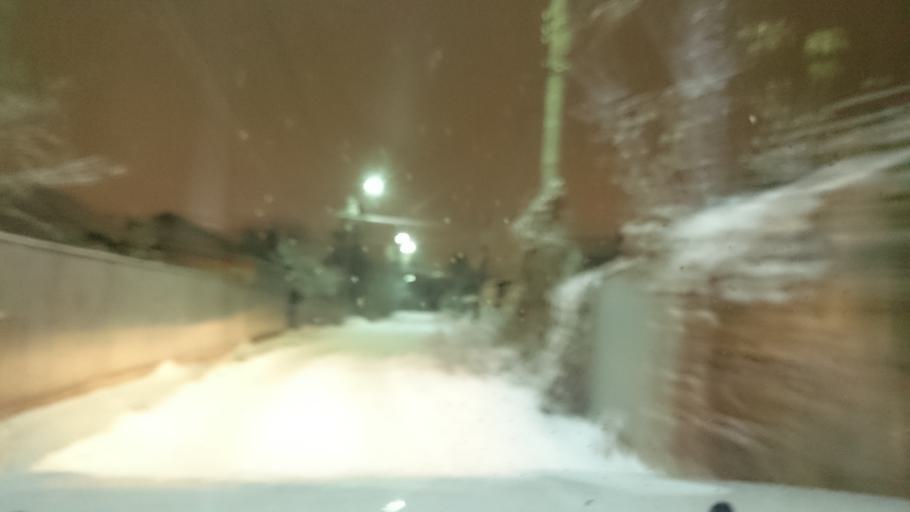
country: RU
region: Tula
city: Tula
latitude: 54.2014
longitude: 37.5647
